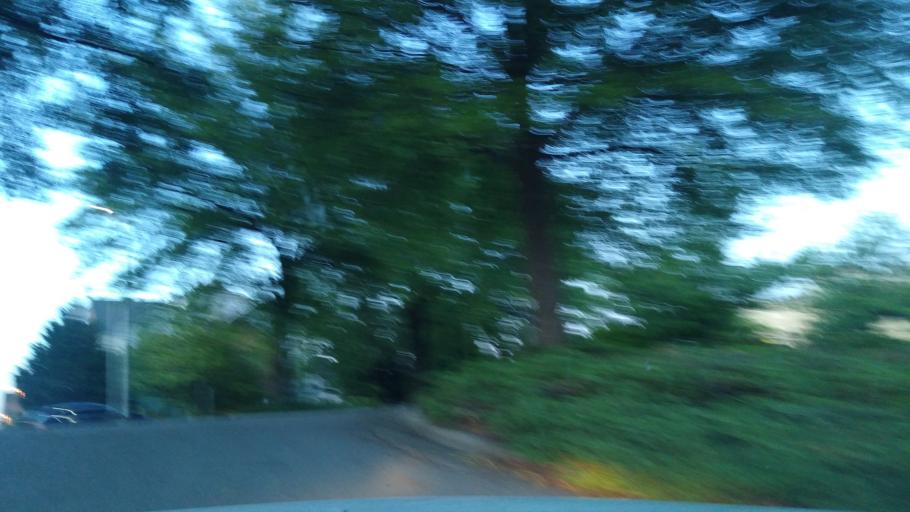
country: US
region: North Carolina
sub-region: Guilford County
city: Oak Ridge
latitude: 36.0829
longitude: -79.9655
